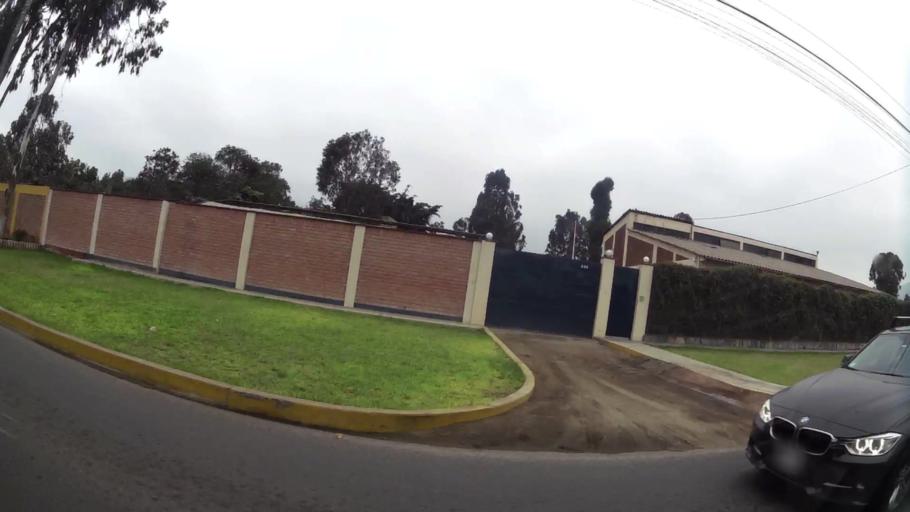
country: PE
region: Lima
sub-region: Lima
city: La Molina
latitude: -12.0816
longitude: -76.9148
